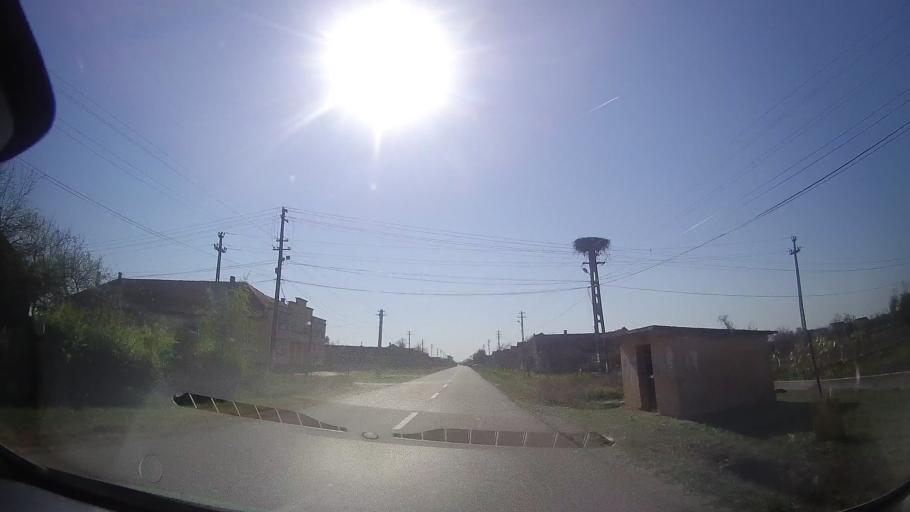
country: RO
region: Timis
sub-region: Comuna Ghizela
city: Ghizela
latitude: 45.8004
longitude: 21.7251
